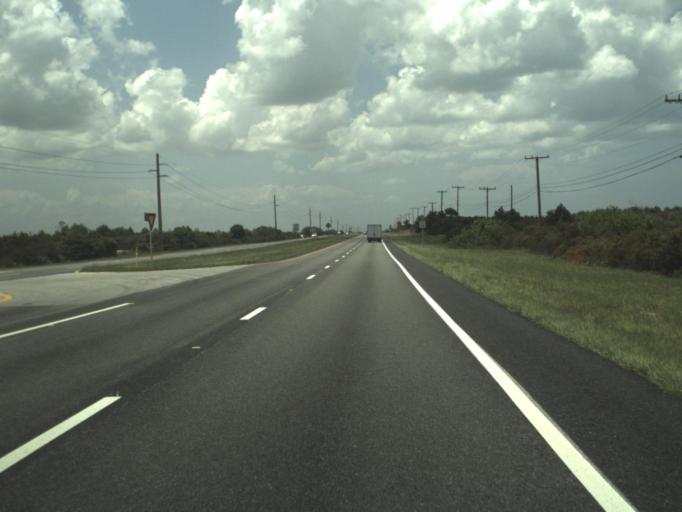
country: US
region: Florida
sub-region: Palm Beach County
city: Tequesta
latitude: 27.0034
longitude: -80.0999
